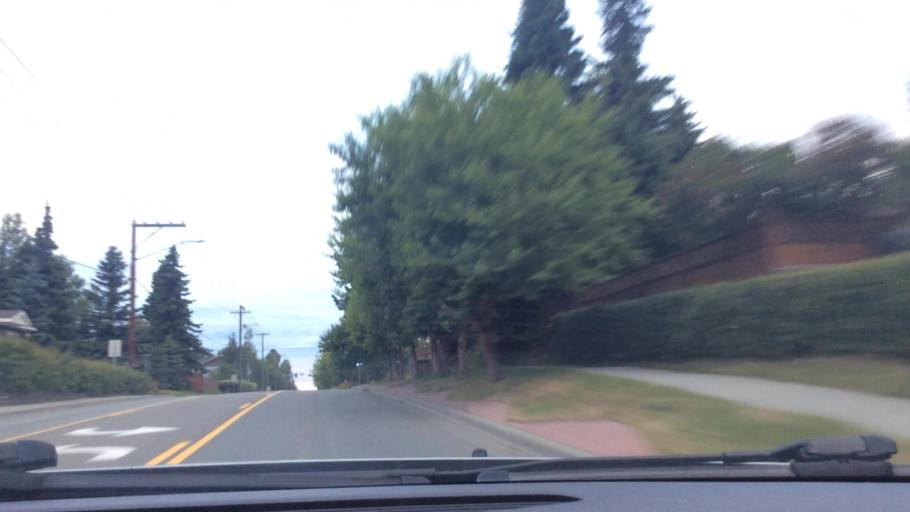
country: US
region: Alaska
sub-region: Anchorage Municipality
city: Anchorage
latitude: 61.2077
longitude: -149.8942
